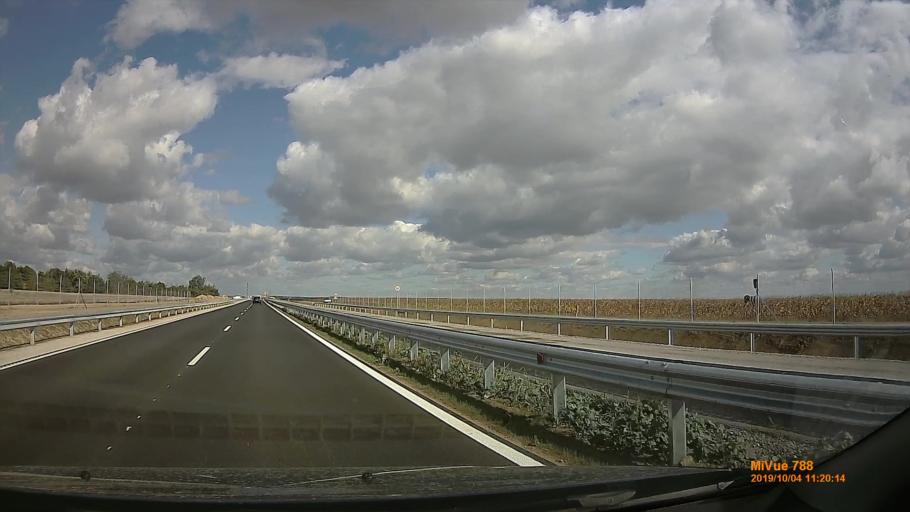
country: HU
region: Somogy
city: Kaposvar
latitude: 46.4944
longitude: 17.8092
